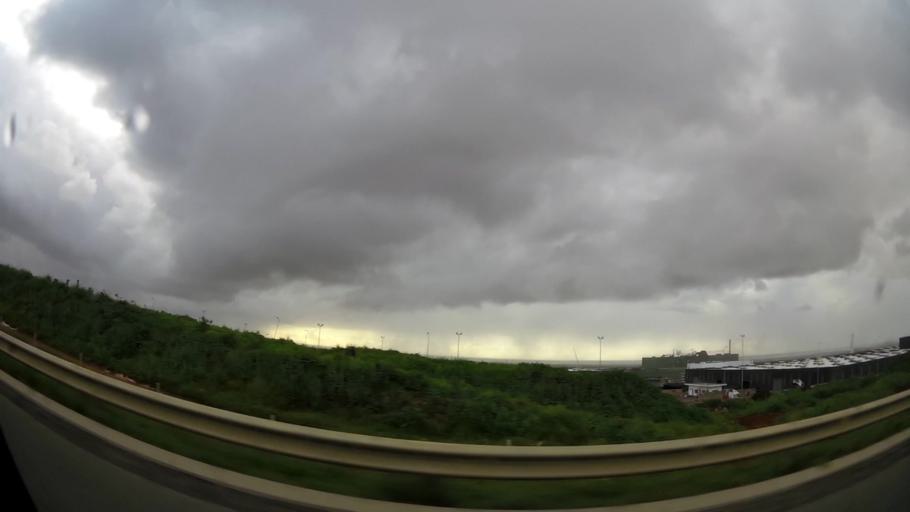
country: MA
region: Grand Casablanca
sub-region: Mohammedia
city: Mohammedia
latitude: 33.6253
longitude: -7.4289
